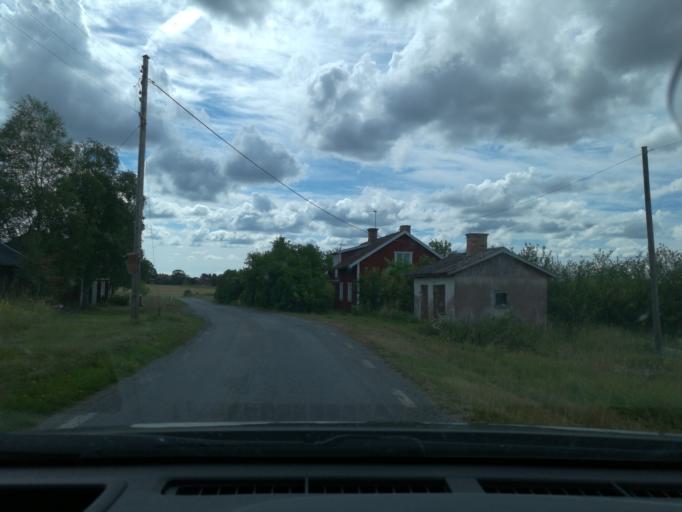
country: SE
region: Stockholm
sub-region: Sigtuna Kommun
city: Marsta
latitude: 59.6523
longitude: 17.8777
